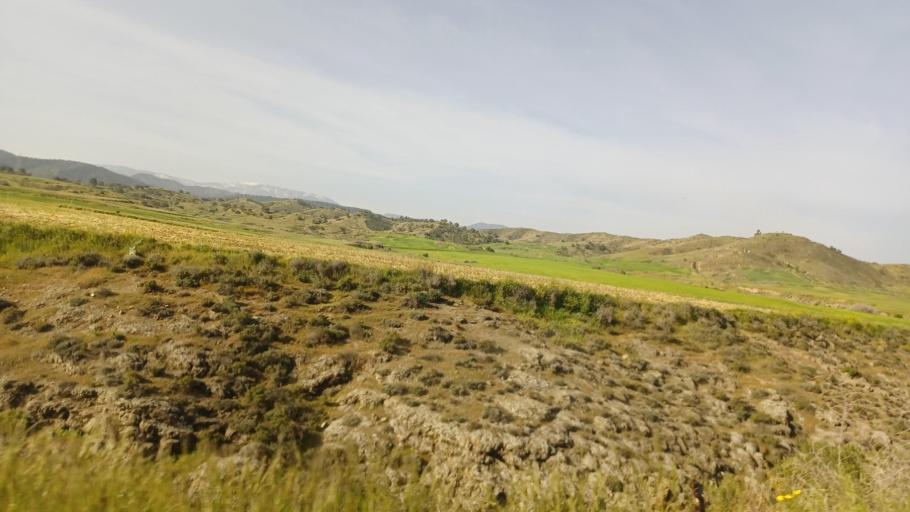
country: CY
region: Lefkosia
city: Lefka
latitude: 35.0891
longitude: 32.9482
